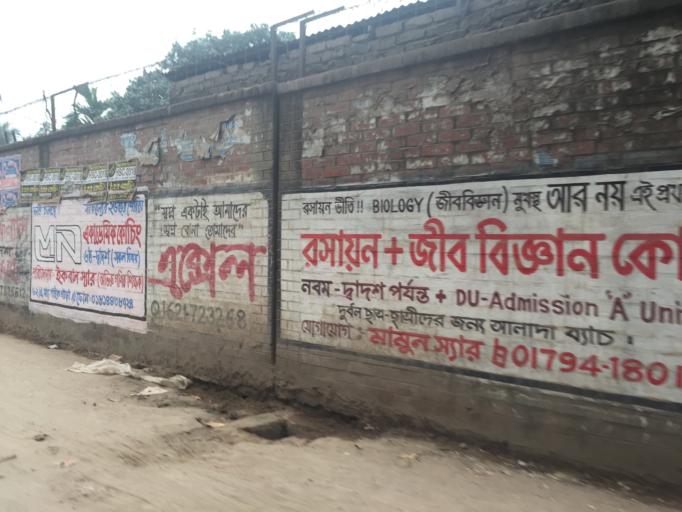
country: BD
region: Dhaka
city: Azimpur
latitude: 23.7868
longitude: 90.3597
